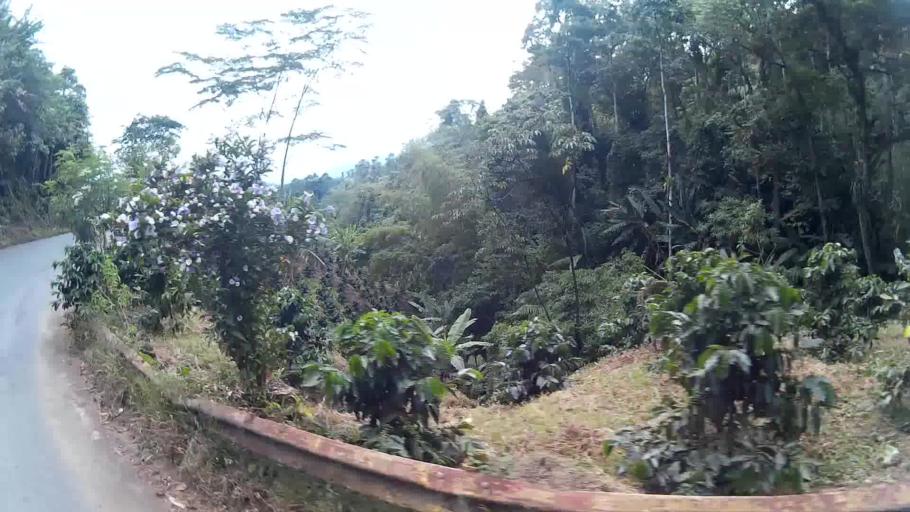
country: CO
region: Risaralda
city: Marsella
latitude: 4.9127
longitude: -75.7353
